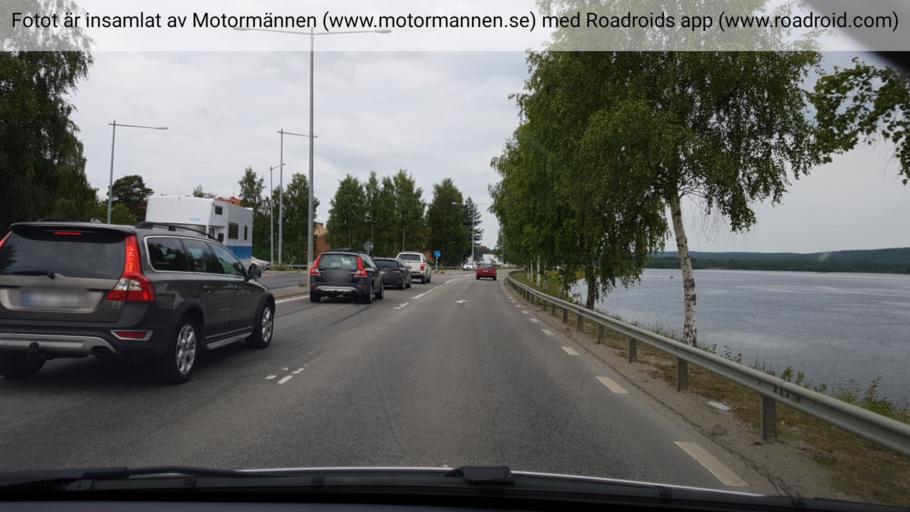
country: SE
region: Vaesterbotten
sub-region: Lycksele Kommun
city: Lycksele
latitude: 64.5918
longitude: 18.6823
